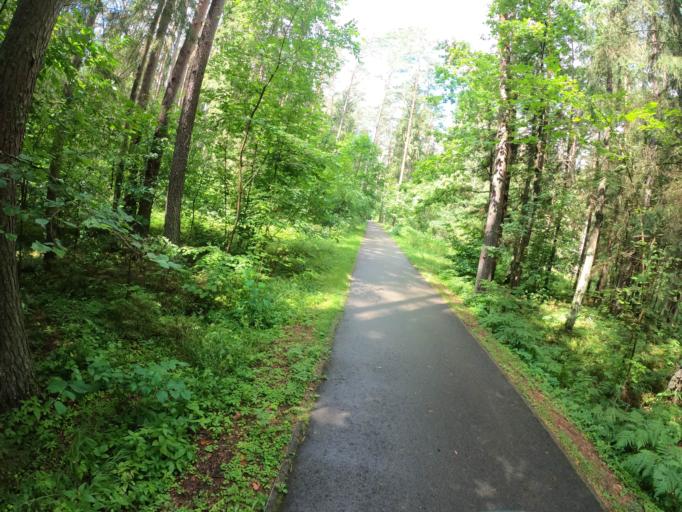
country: LT
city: Prienai
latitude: 54.6340
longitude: 23.9842
